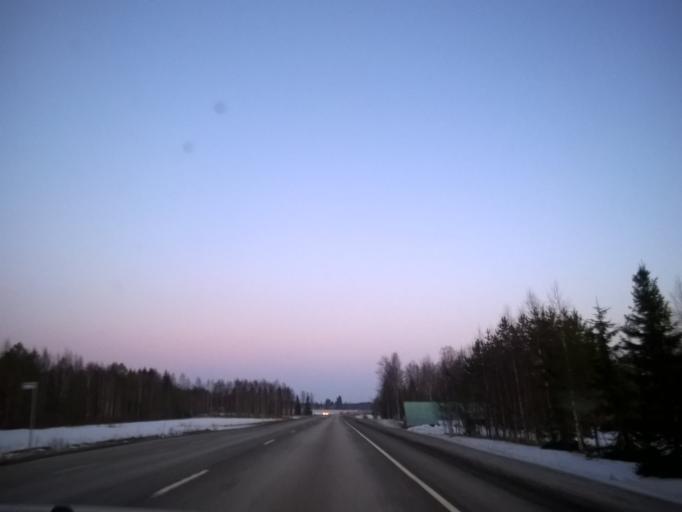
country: FI
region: Northern Ostrobothnia
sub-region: Nivala-Haapajaervi
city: Pyhaejaervi
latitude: 63.8302
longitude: 25.8743
